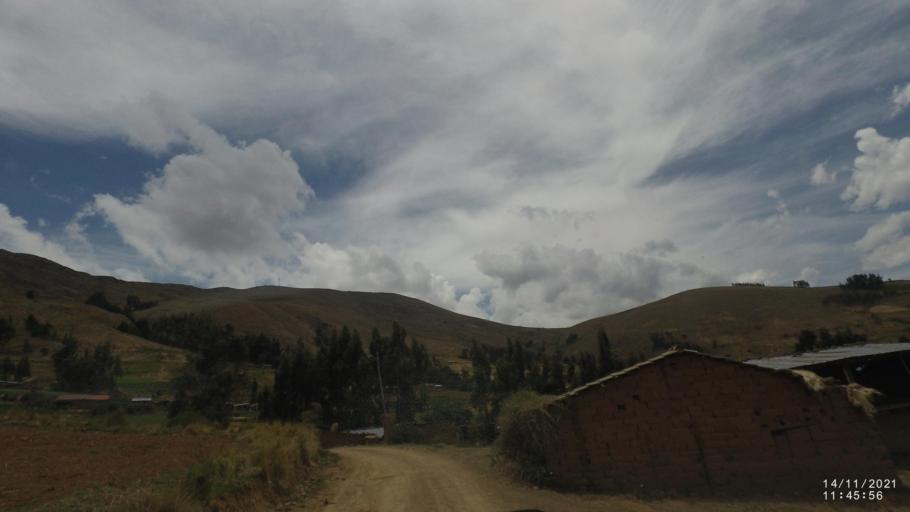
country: BO
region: Cochabamba
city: Colomi
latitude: -17.3532
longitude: -65.9880
